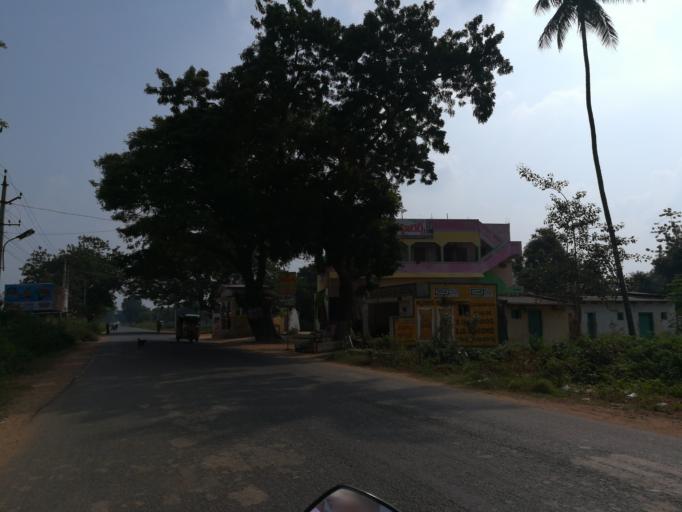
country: IN
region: Andhra Pradesh
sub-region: Nellore
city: Kovur
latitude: 14.5516
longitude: 79.9906
